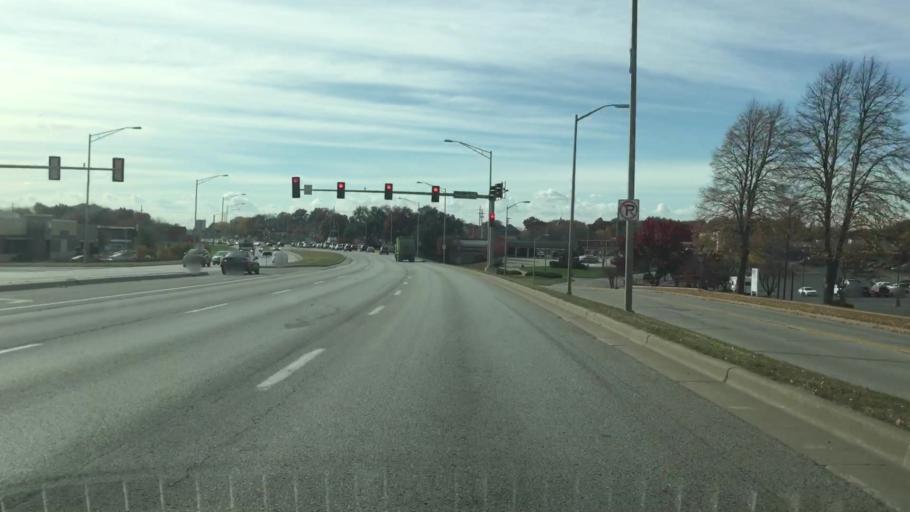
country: US
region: Kansas
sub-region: Johnson County
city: Shawnee
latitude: 39.0144
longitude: -94.7380
